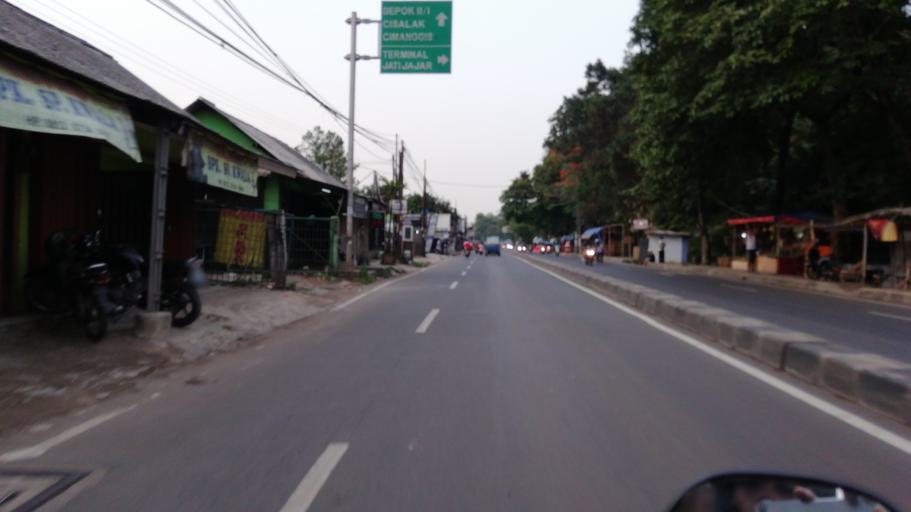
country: ID
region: West Java
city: Depok
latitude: -6.4265
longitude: 106.8566
